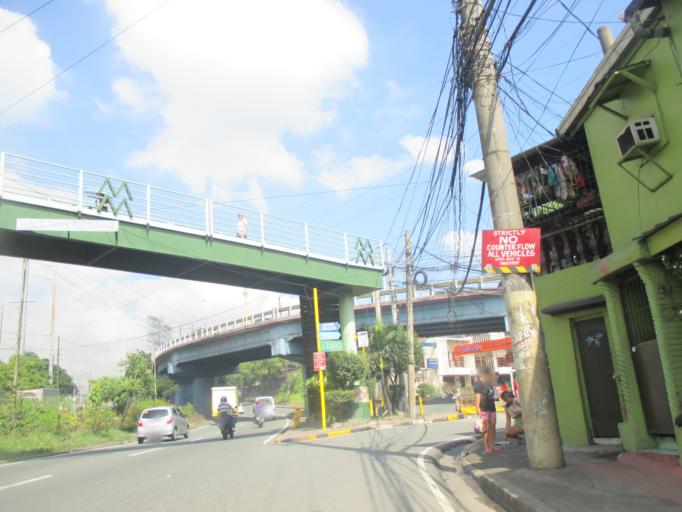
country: PH
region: Metro Manila
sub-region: Marikina
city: Calumpang
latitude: 14.6314
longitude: 121.0785
